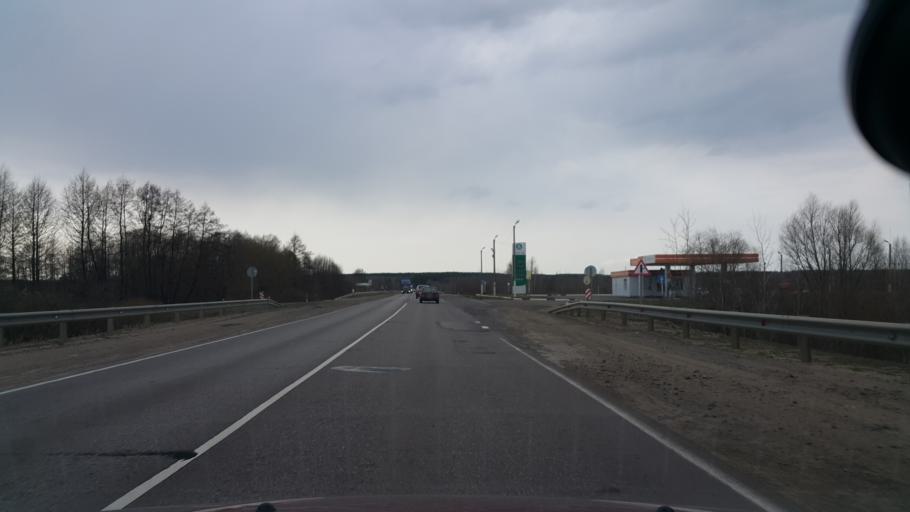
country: RU
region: Tambov
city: Znamenka
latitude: 52.5211
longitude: 41.3630
